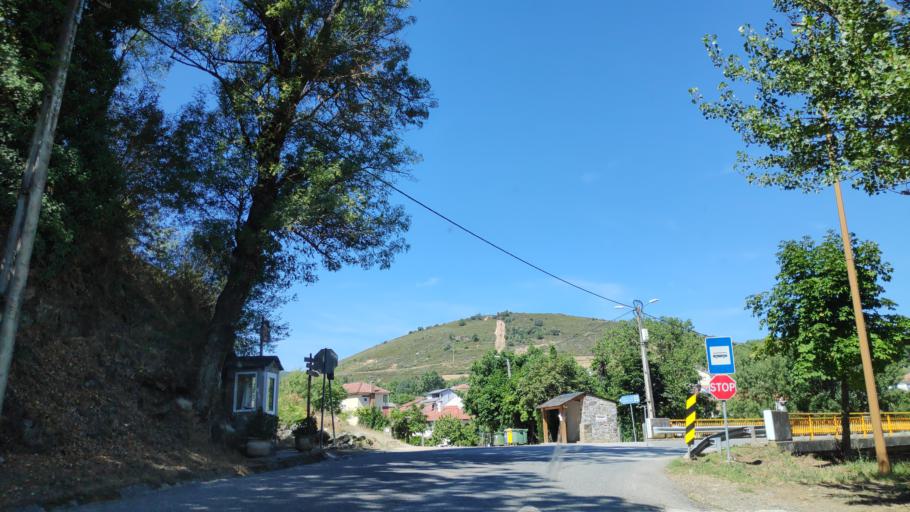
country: PT
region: Braganca
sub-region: Braganca Municipality
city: Braganca
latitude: 41.8689
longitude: -6.7515
